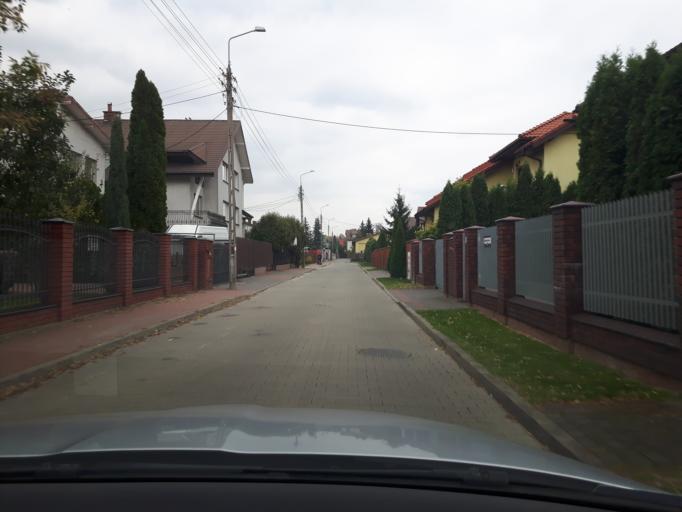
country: PL
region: Masovian Voivodeship
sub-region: Powiat wolominski
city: Zabki
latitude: 52.2911
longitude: 21.1055
